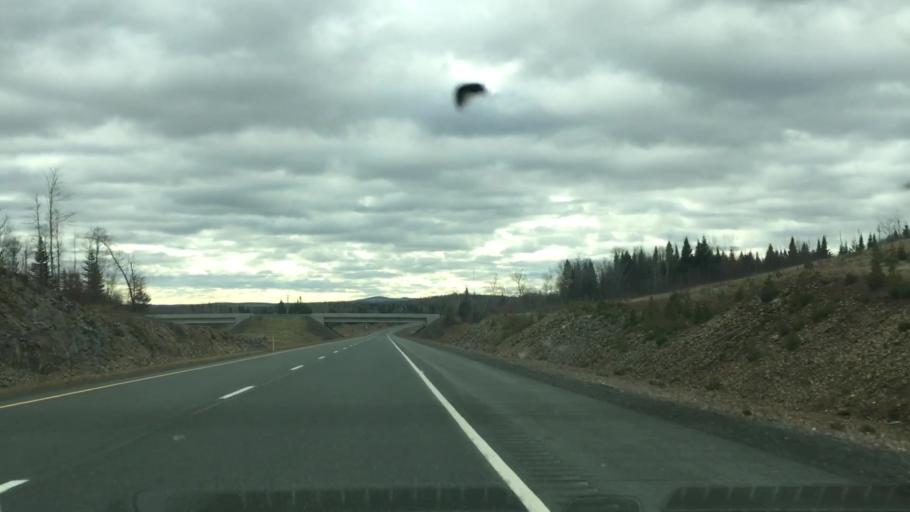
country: US
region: Maine
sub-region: Aroostook County
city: Easton
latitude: 46.6287
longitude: -67.7409
